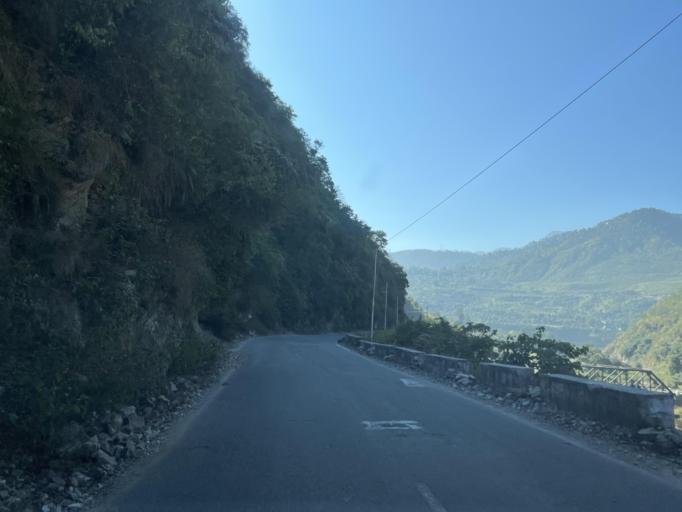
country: IN
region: Uttarakhand
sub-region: Naini Tal
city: Naini Tal
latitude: 29.5168
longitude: 79.4798
